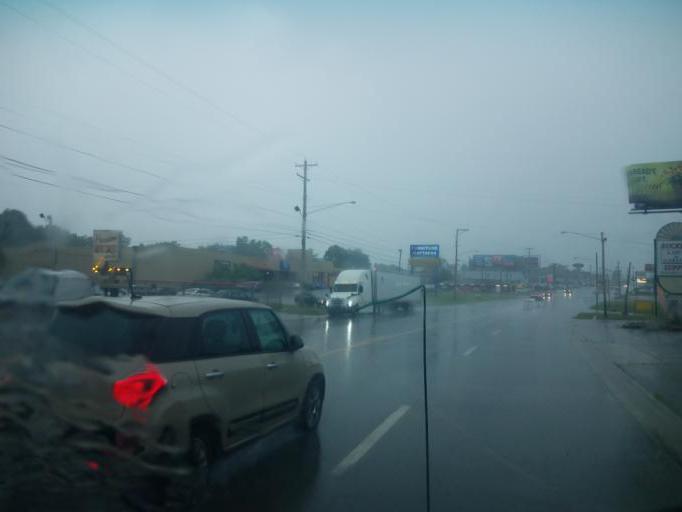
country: US
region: Ohio
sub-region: Stark County
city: Genoa
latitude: 40.7923
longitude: -81.4504
